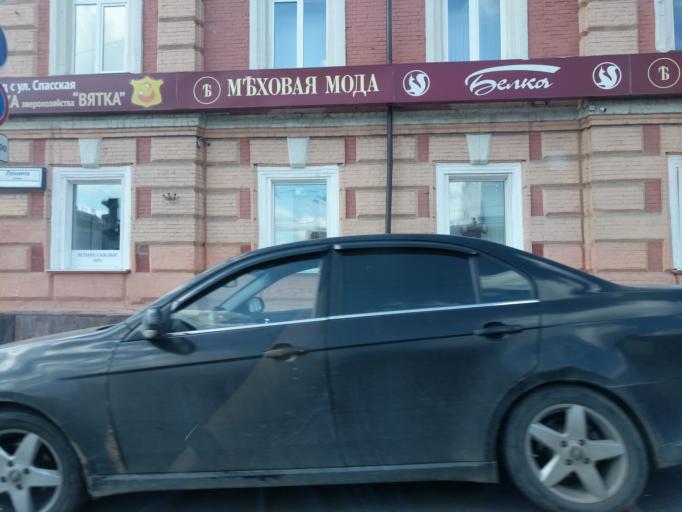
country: RU
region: Kirov
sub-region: Kirovo-Chepetskiy Rayon
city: Kirov
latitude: 58.6025
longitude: 49.6809
